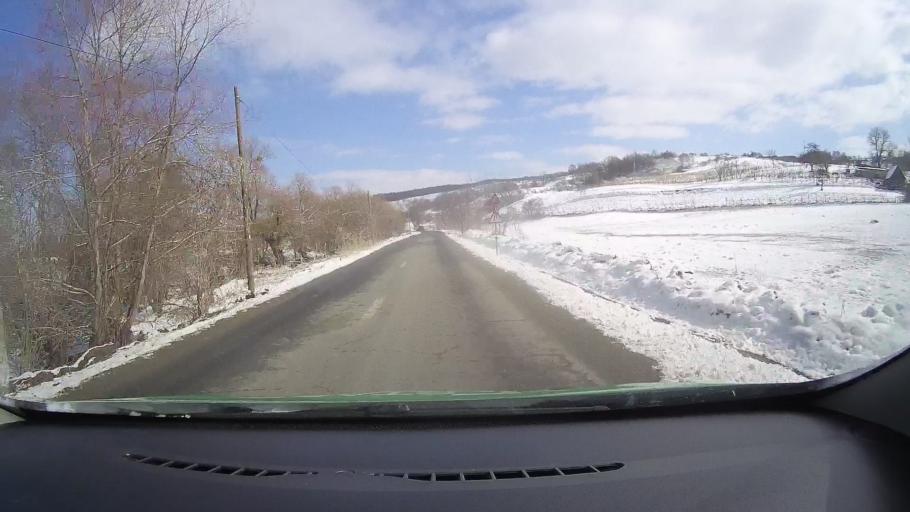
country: RO
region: Sibiu
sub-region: Comuna Mihaileni
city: Mihaileni
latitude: 45.9926
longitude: 24.3500
